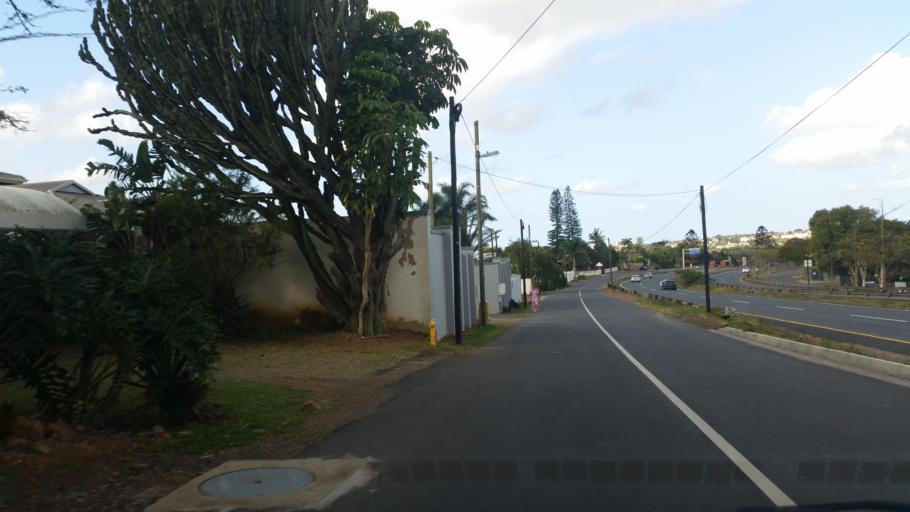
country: ZA
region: KwaZulu-Natal
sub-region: eThekwini Metropolitan Municipality
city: Berea
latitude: -29.8300
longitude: 30.9488
